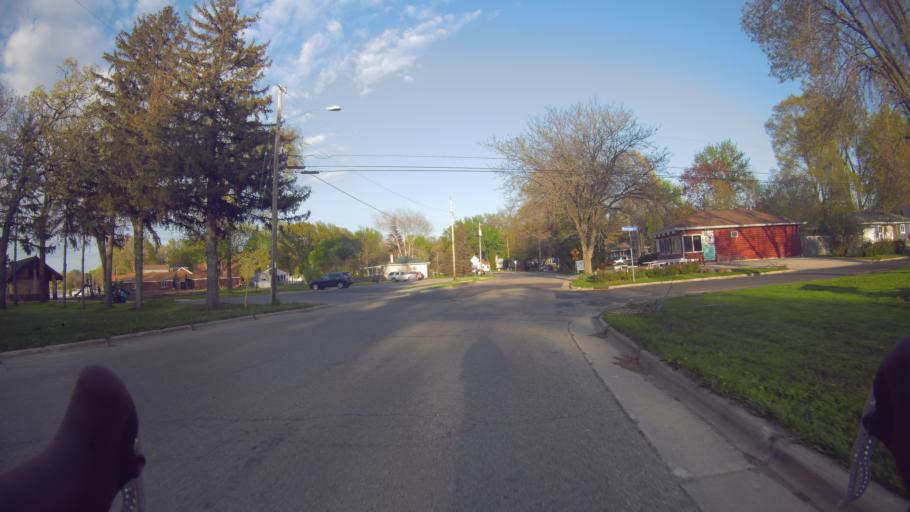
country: US
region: Wisconsin
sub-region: Dane County
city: Monona
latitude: 43.0716
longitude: -89.3343
